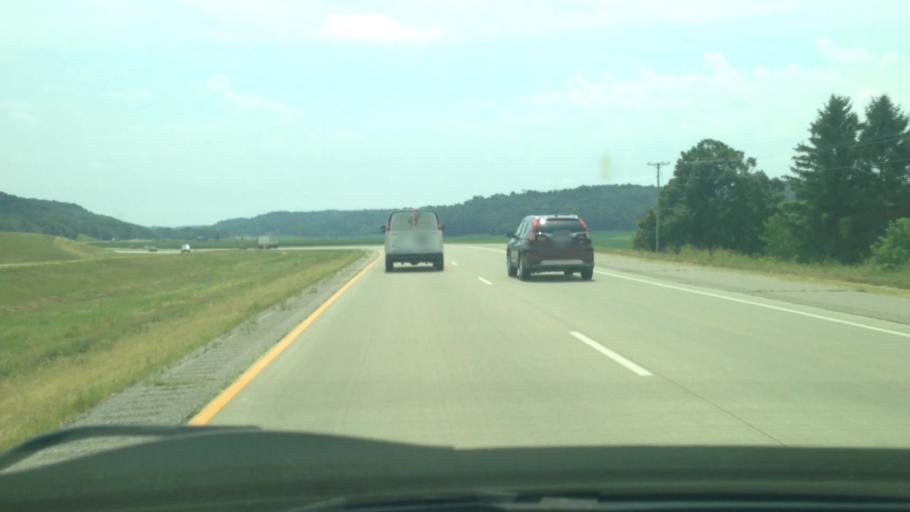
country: US
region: Wisconsin
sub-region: Sauk County
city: Sauk City
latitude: 43.2429
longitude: -89.6952
